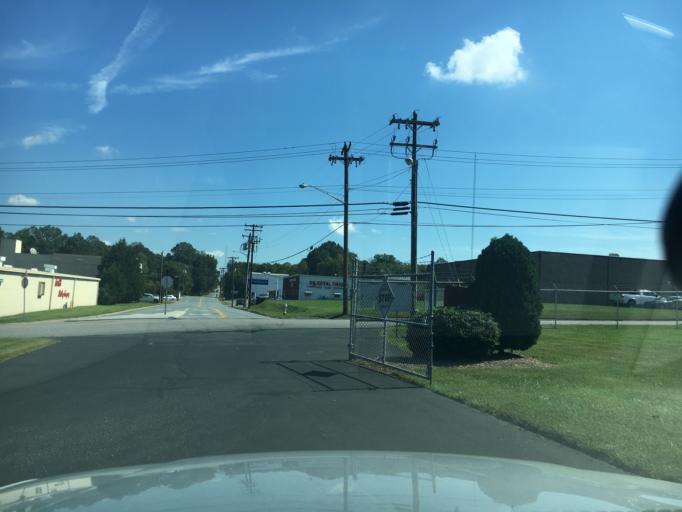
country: US
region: North Carolina
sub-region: Catawba County
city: Hickory
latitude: 35.7332
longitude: -81.3527
